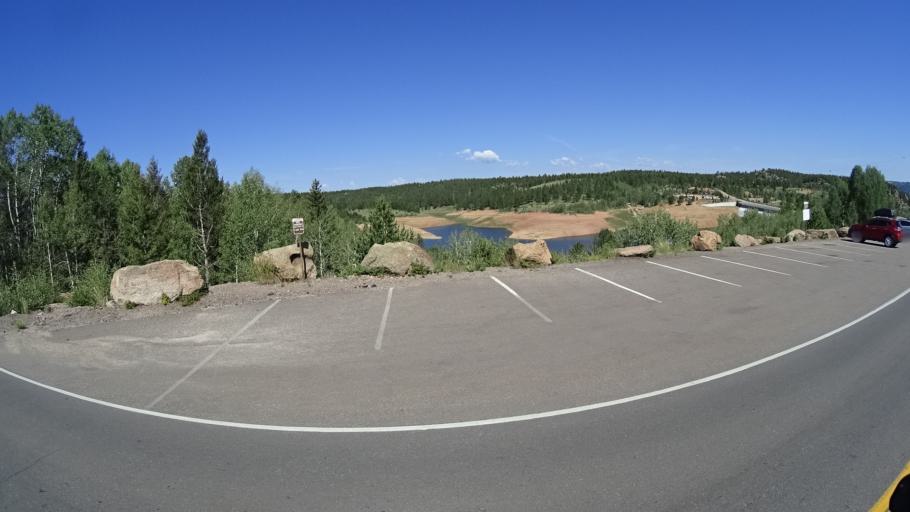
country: US
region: Colorado
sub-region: El Paso County
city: Cascade-Chipita Park
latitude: 38.9173
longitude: -105.0226
